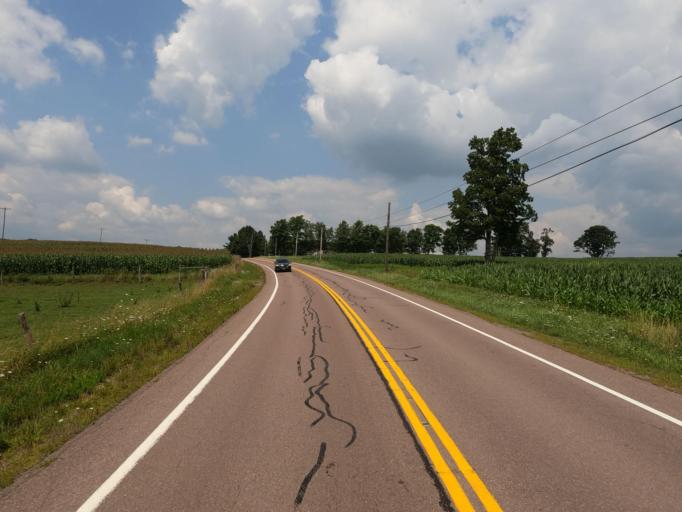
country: US
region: Maryland
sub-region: Allegany County
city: Westernport
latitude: 39.6174
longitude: -79.2141
